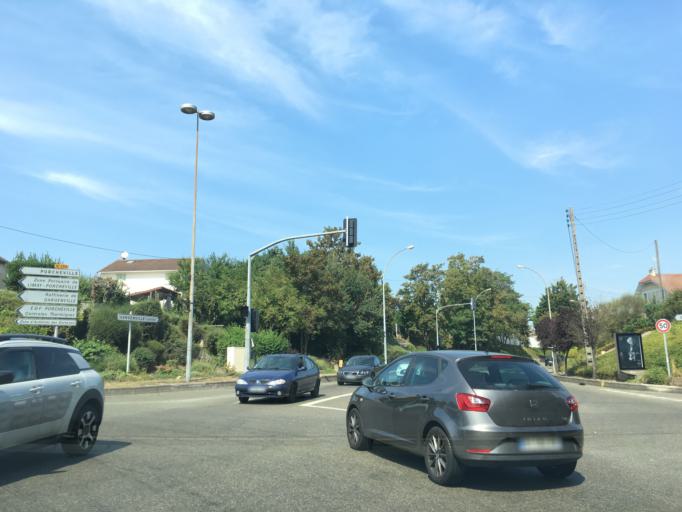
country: FR
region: Ile-de-France
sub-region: Departement des Yvelines
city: Gargenville
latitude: 48.9753
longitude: 1.8068
